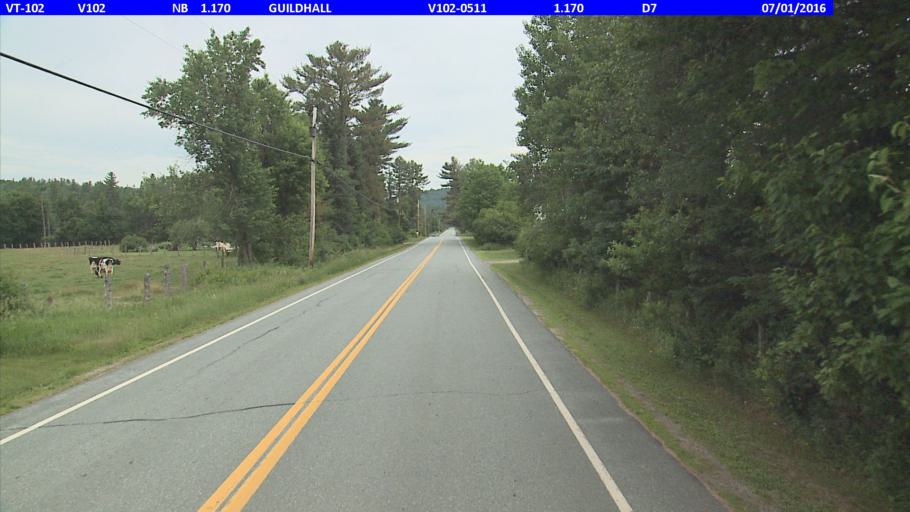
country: US
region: New Hampshire
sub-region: Coos County
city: Lancaster
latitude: 44.5122
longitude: -71.5940
